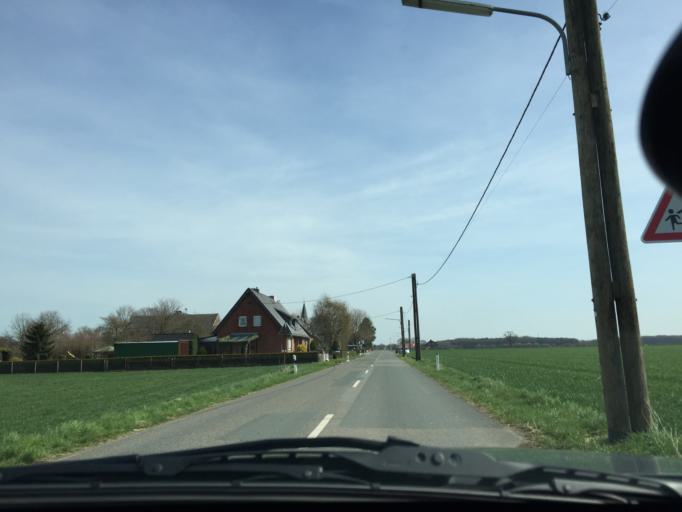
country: DE
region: North Rhine-Westphalia
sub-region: Regierungsbezirk Dusseldorf
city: Goch
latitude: 51.6475
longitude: 6.1471
